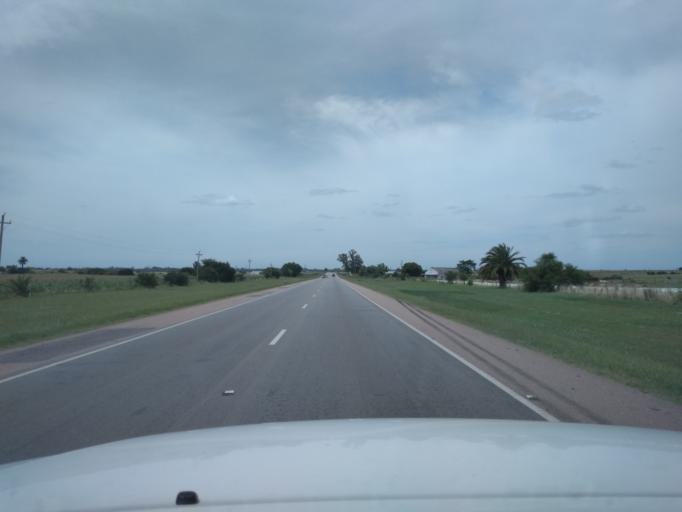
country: UY
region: Canelones
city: Canelones
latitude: -34.3945
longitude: -56.2556
